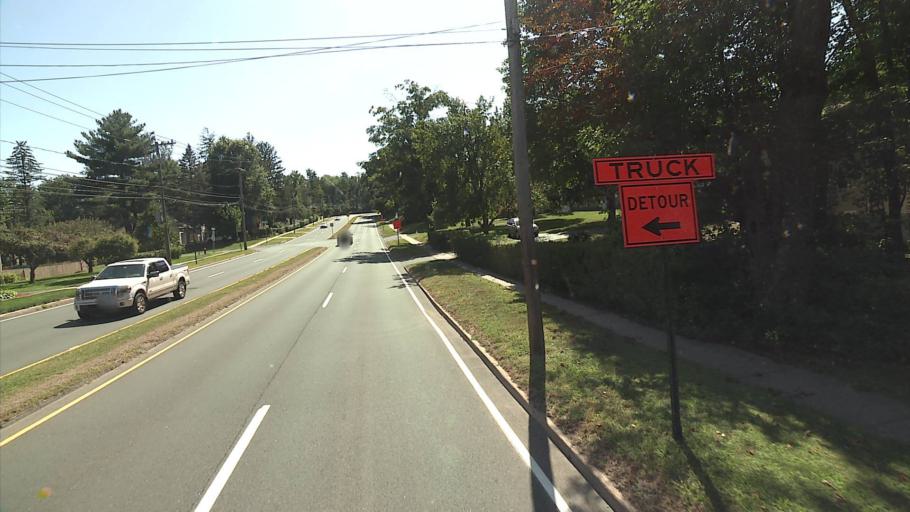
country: US
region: Connecticut
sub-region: Hartford County
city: Windsor
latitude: 41.8440
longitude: -72.6479
